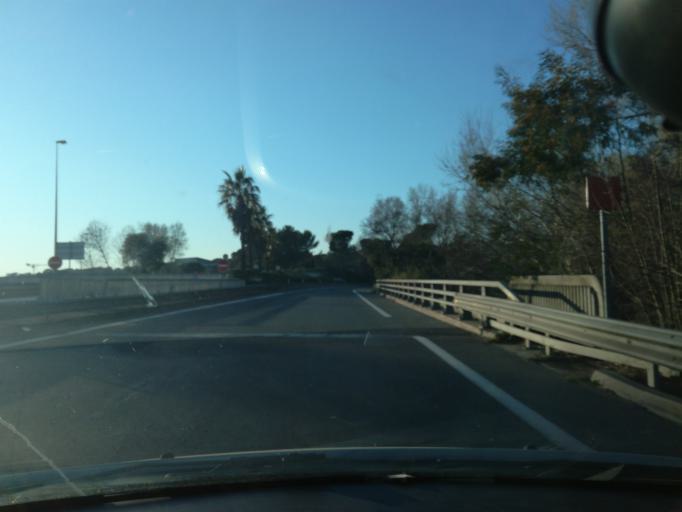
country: FR
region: Provence-Alpes-Cote d'Azur
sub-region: Departement du Var
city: Frejus
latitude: 43.4727
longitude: 6.7427
